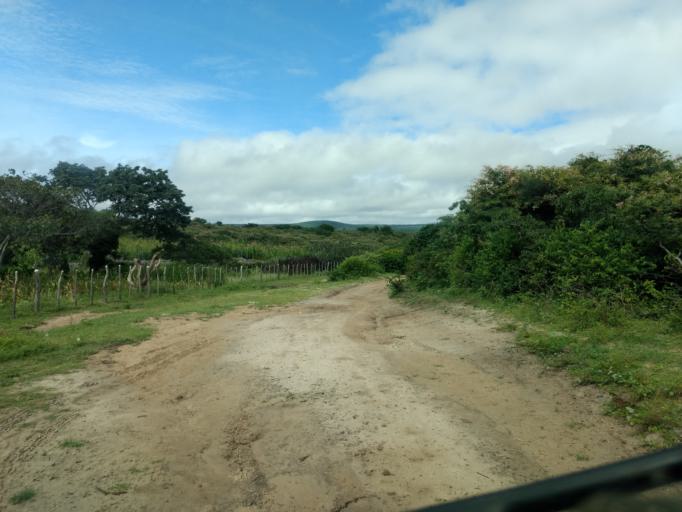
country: BR
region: Ceara
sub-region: Crateus
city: Crateus
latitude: -5.1958
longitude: -40.9505
